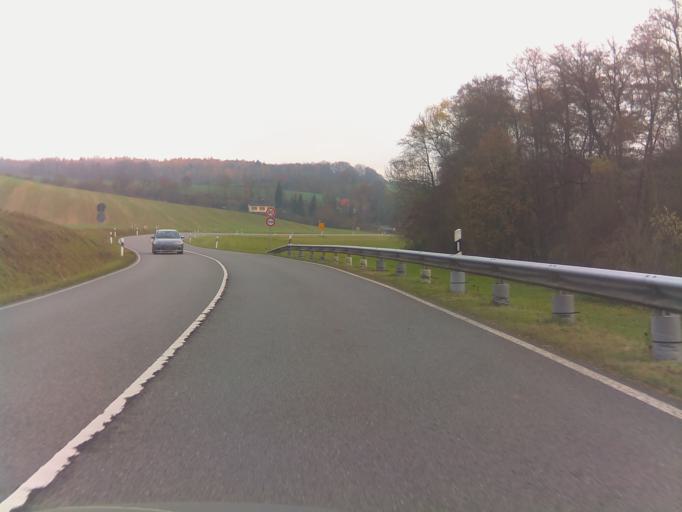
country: DE
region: Baden-Wuerttemberg
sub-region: Karlsruhe Region
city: Wiesenbach
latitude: 49.3615
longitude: 8.8308
